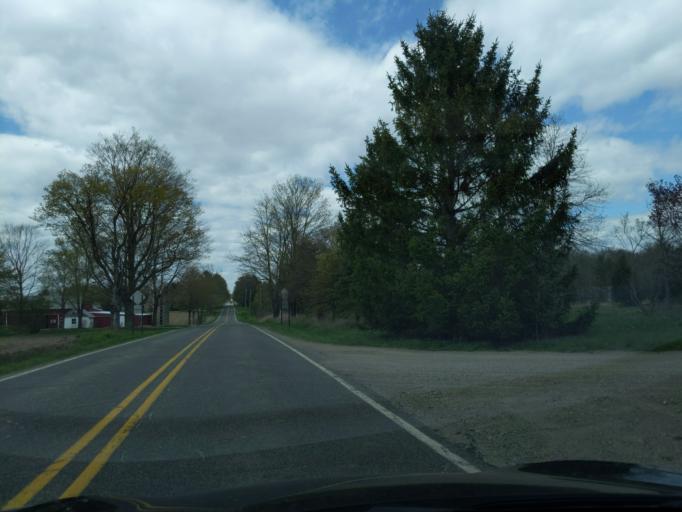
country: US
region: Michigan
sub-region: Ingham County
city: Holt
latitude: 42.6343
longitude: -84.4626
